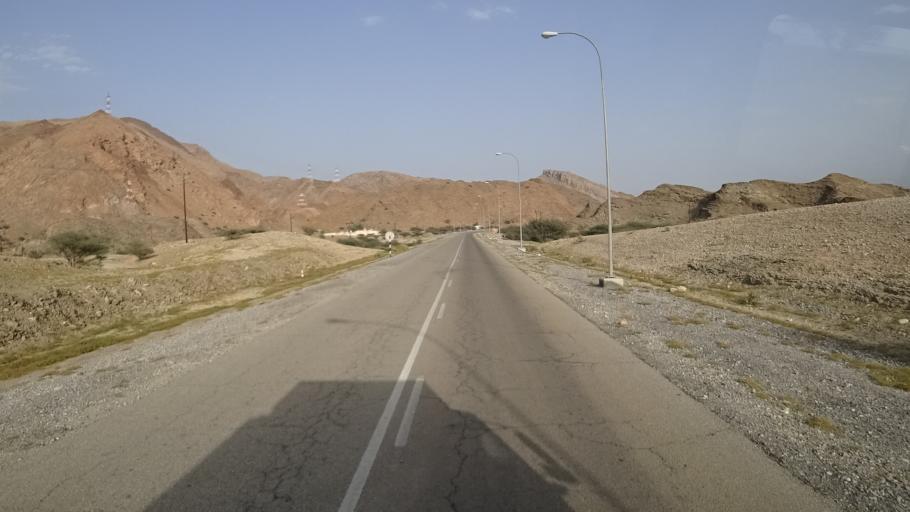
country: OM
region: Muhafazat Masqat
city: Bawshar
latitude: 23.3707
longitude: 58.5208
